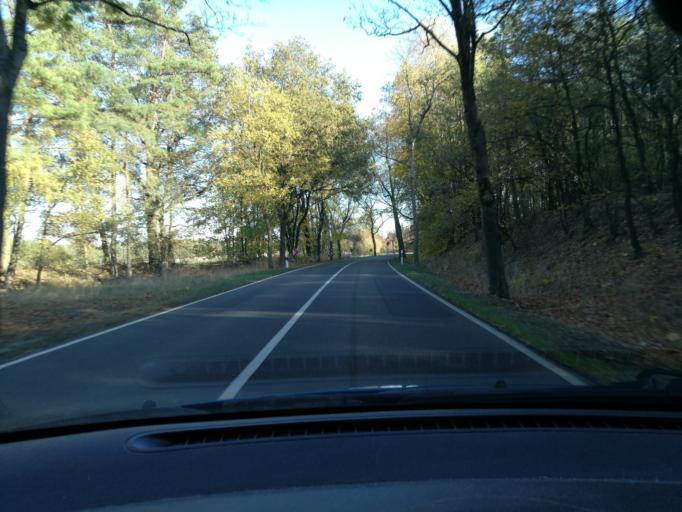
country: DE
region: Brandenburg
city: Karstadt
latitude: 53.1654
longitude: 11.6720
